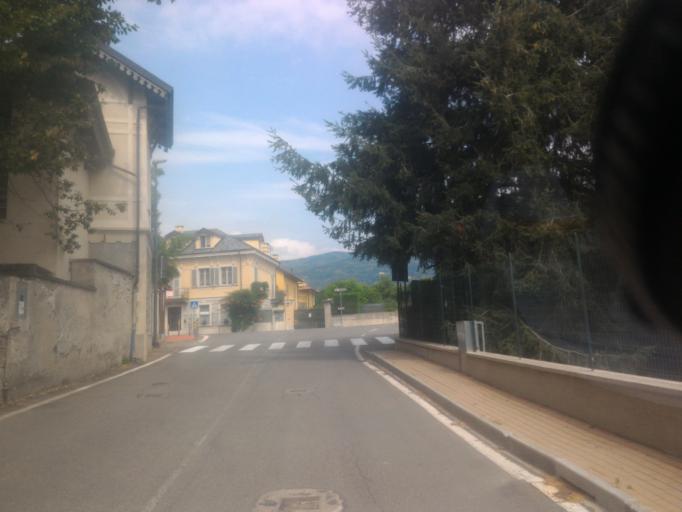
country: IT
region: Piedmont
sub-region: Provincia di Torino
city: San Secondo di Pinerolo
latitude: 44.8741
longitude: 7.3100
